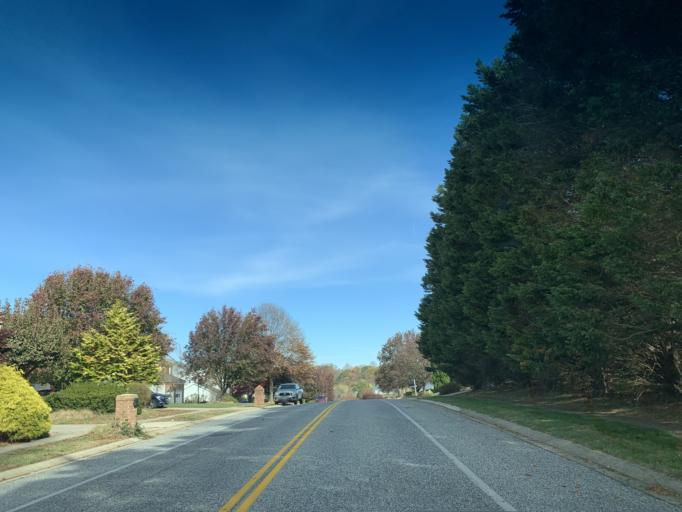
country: US
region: Maryland
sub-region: Harford County
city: South Bel Air
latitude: 39.5252
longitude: -76.3229
